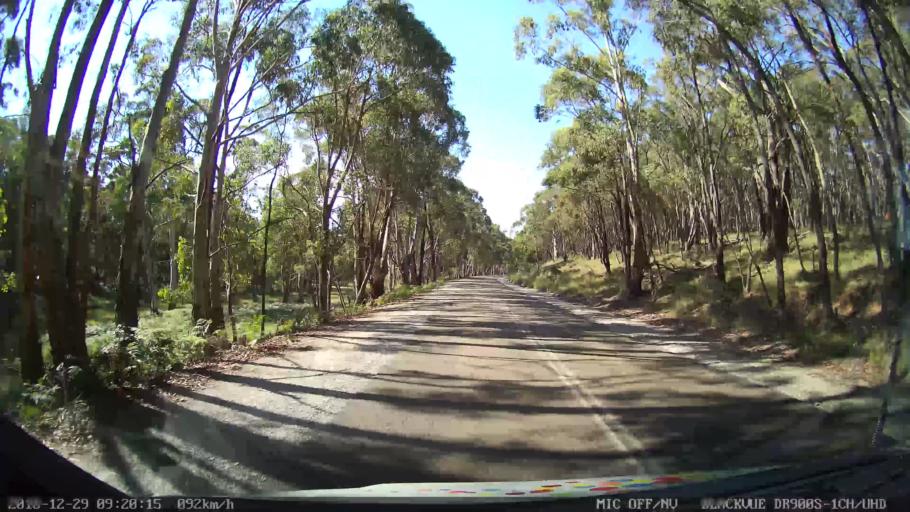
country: AU
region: New South Wales
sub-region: Upper Lachlan Shire
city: Crookwell
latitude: -34.4901
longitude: 149.4244
